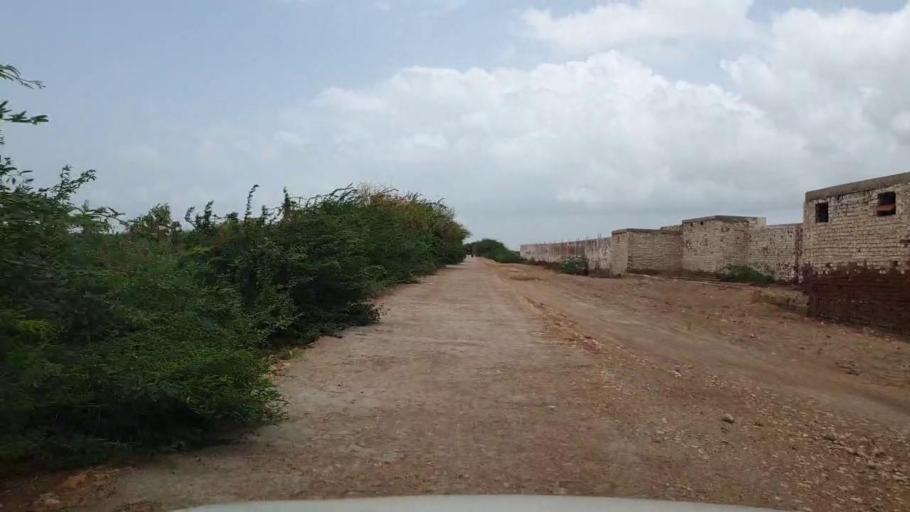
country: PK
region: Sindh
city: Kario
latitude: 24.6909
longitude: 68.6631
